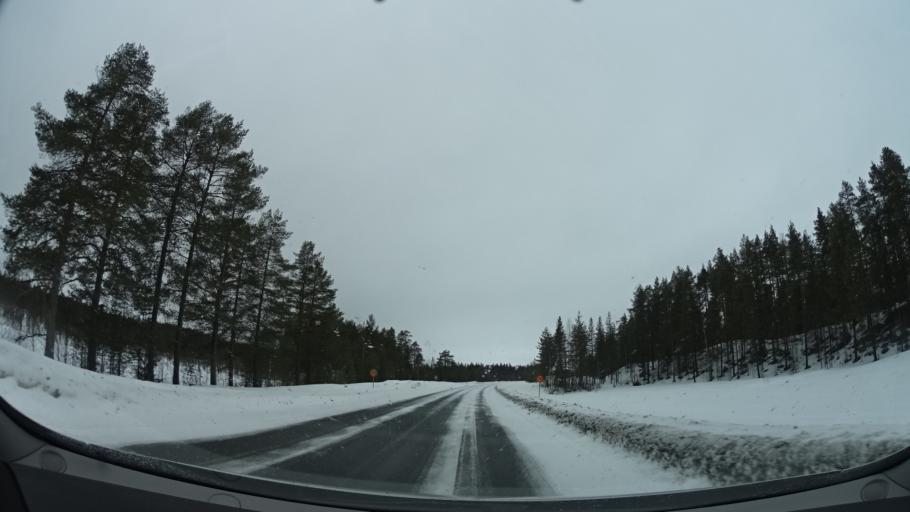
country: SE
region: Vaesterbotten
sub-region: Mala Kommun
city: Mala
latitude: 65.1563
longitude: 18.7917
